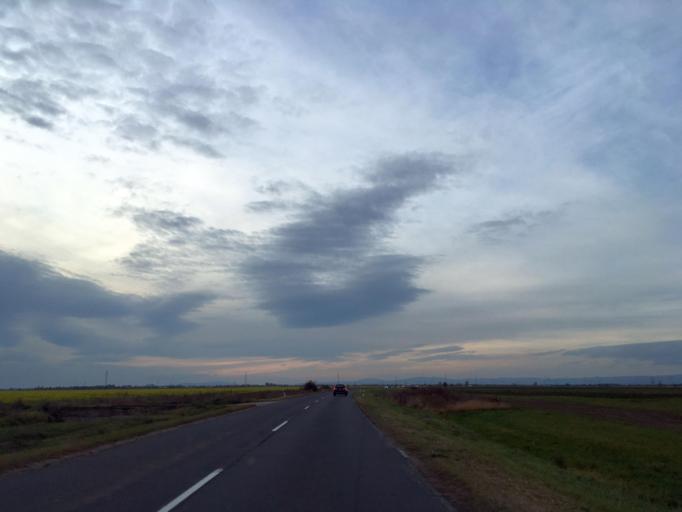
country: SK
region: Trnavsky
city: Samorin
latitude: 48.1042
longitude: 17.3415
